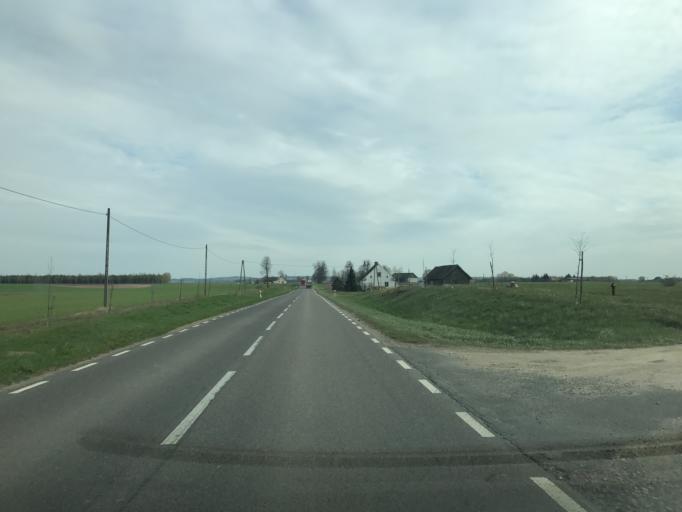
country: PL
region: Warmian-Masurian Voivodeship
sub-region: Powiat ostrodzki
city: Gierzwald
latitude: 53.5089
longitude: 20.0833
